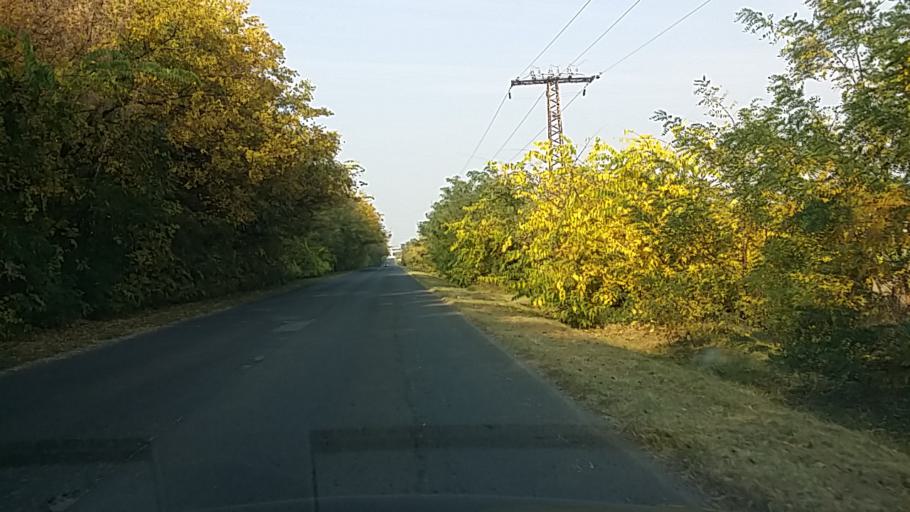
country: HU
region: Pest
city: Fot
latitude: 47.6137
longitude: 19.1621
